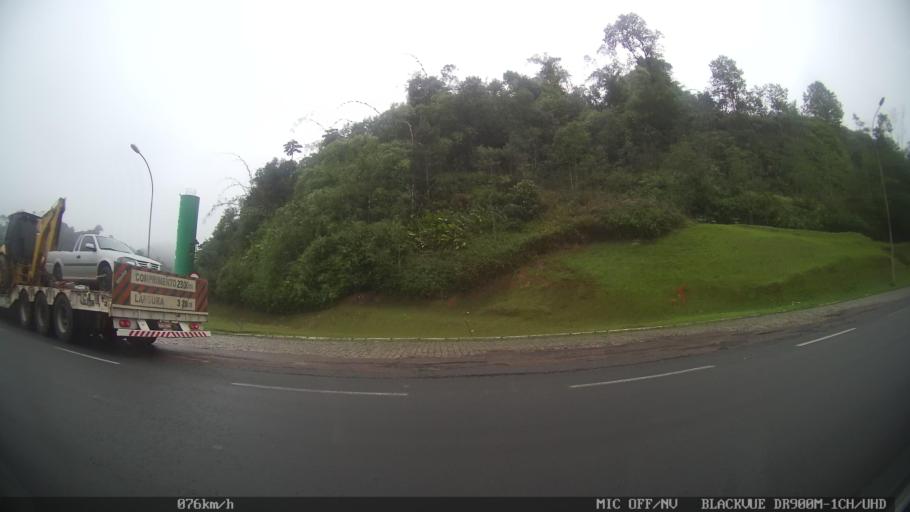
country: BR
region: Parana
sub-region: Antonina
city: Antonina
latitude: -25.1028
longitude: -48.7224
